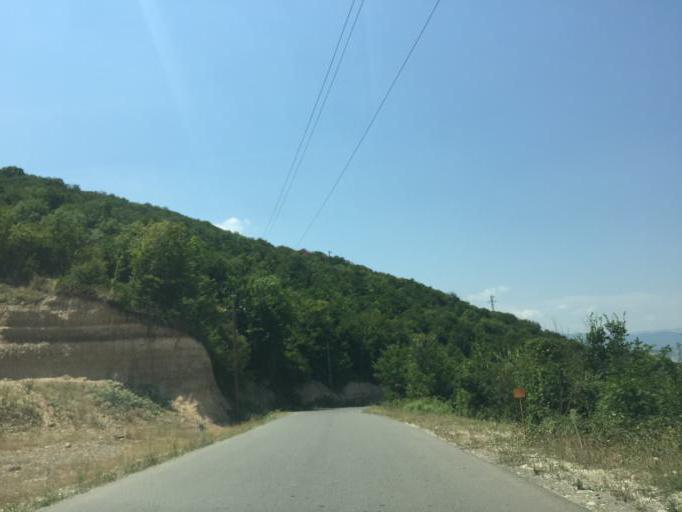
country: AZ
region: Tartar Rayon
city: Martakert
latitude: 40.1436
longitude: 46.5664
